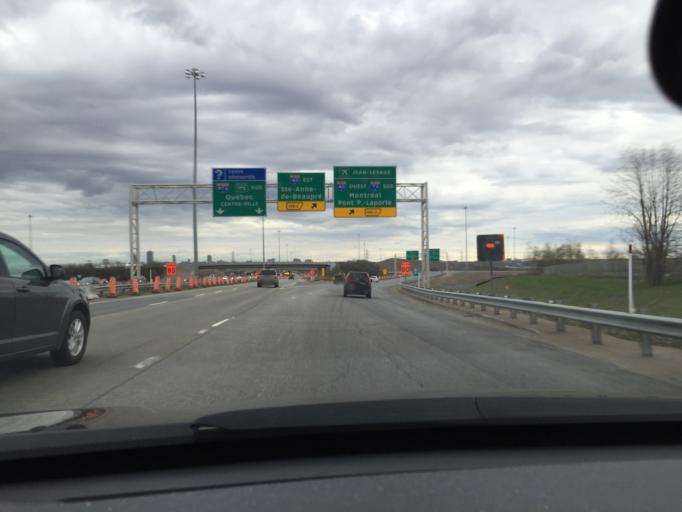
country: CA
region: Quebec
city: Quebec
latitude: 46.8409
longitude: -71.2678
